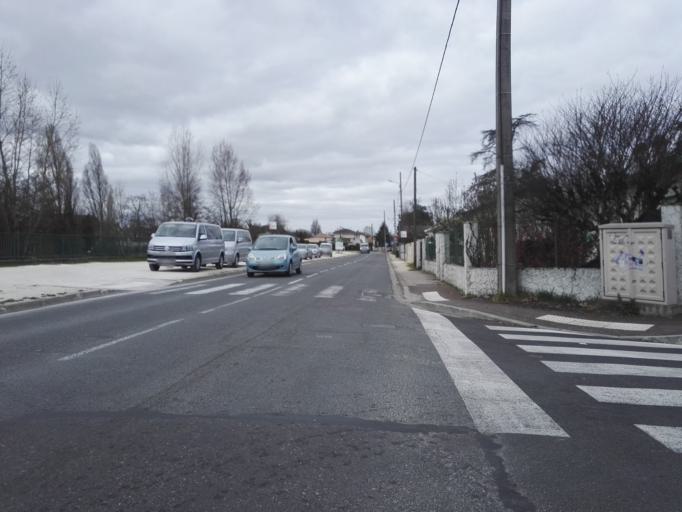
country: FR
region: Aquitaine
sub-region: Departement de la Gironde
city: Villenave-d'Ornon
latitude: 44.7864
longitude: -0.5714
